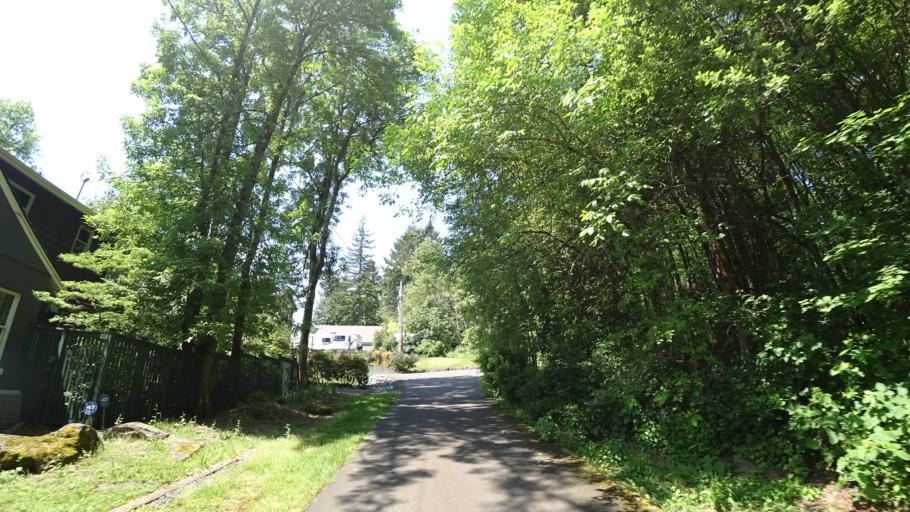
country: US
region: Oregon
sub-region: Washington County
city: Metzger
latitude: 45.4425
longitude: -122.7174
